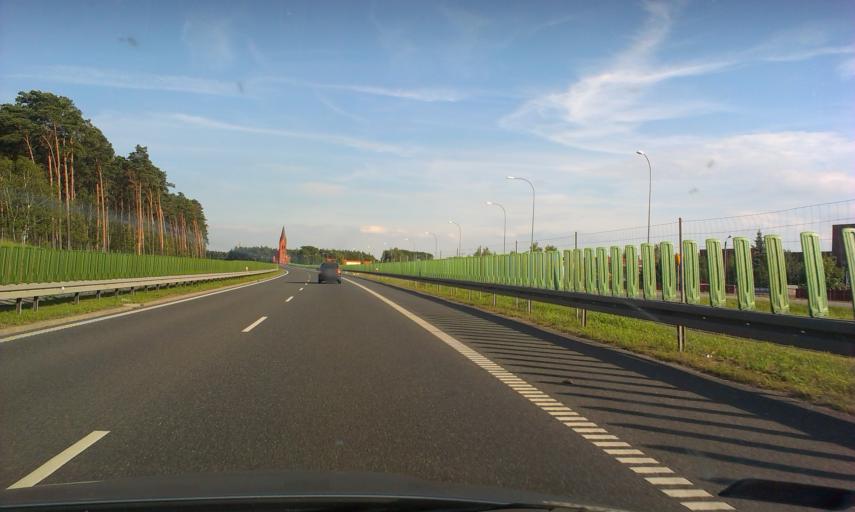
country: PL
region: Kujawsko-Pomorskie
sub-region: Powiat bydgoski
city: Biale Blota
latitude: 53.0766
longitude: 17.9138
